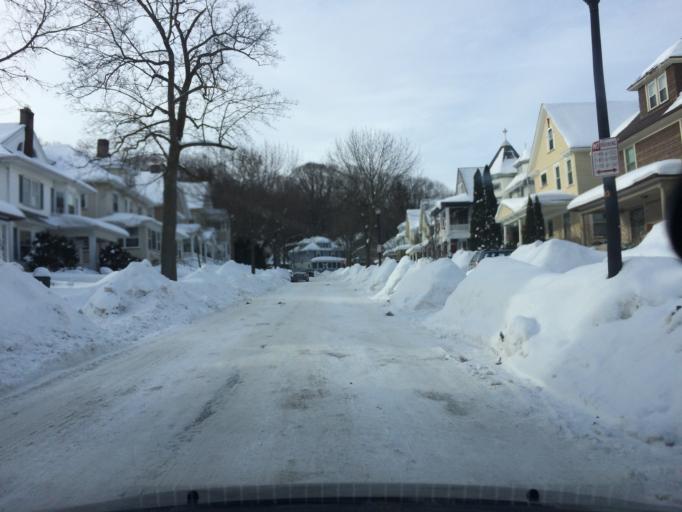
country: US
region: New York
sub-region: Monroe County
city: Rochester
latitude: 43.1372
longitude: -77.5881
